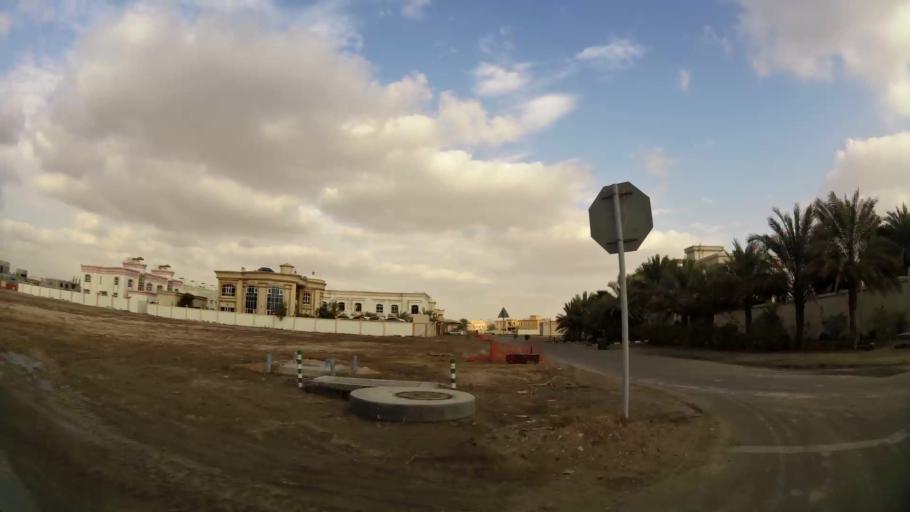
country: AE
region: Abu Dhabi
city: Abu Dhabi
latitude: 24.3654
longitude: 54.5493
